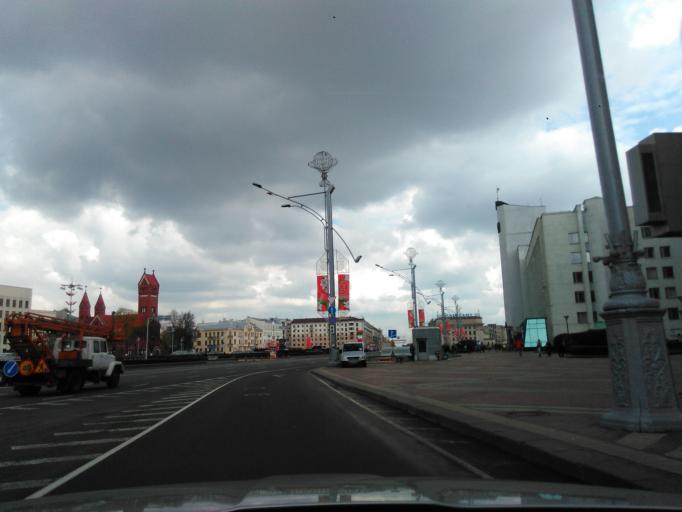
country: BY
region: Minsk
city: Minsk
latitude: 53.8940
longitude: 27.5458
